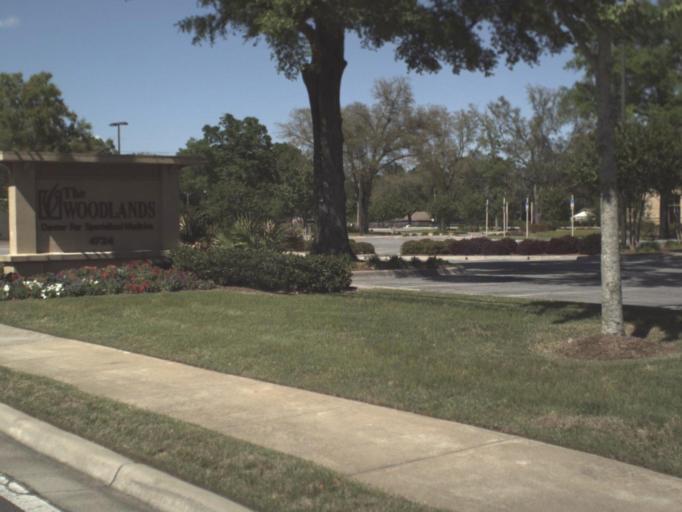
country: US
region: Florida
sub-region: Escambia County
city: Brent
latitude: 30.4657
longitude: -87.2242
